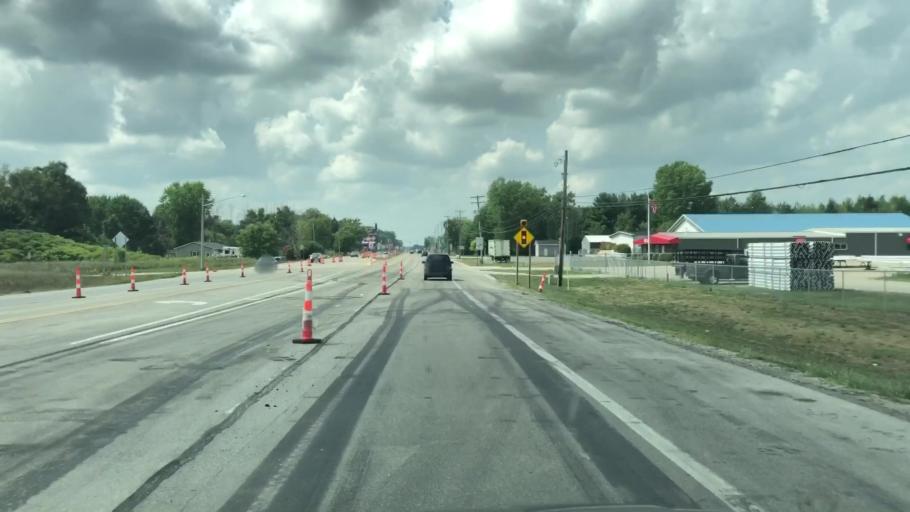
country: US
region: Michigan
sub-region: Isabella County
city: Mount Pleasant
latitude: 43.6117
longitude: -84.7025
